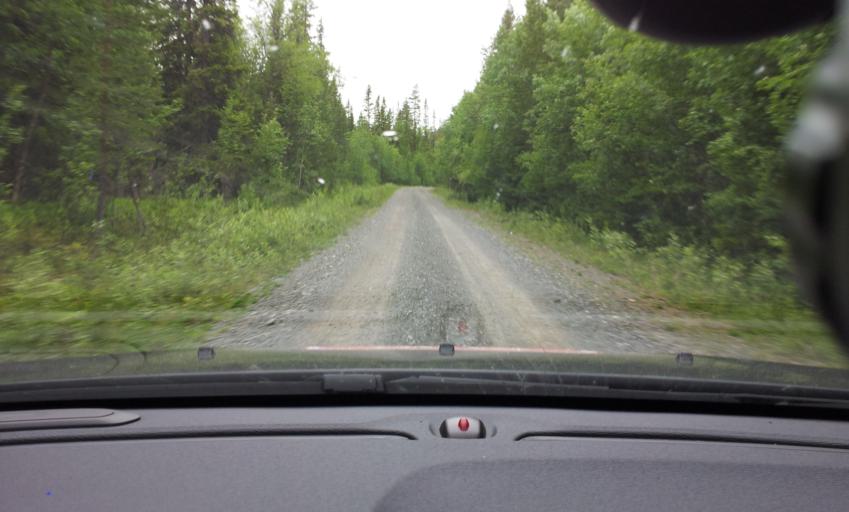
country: SE
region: Jaemtland
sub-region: Are Kommun
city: Jarpen
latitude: 63.1739
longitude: 13.5566
